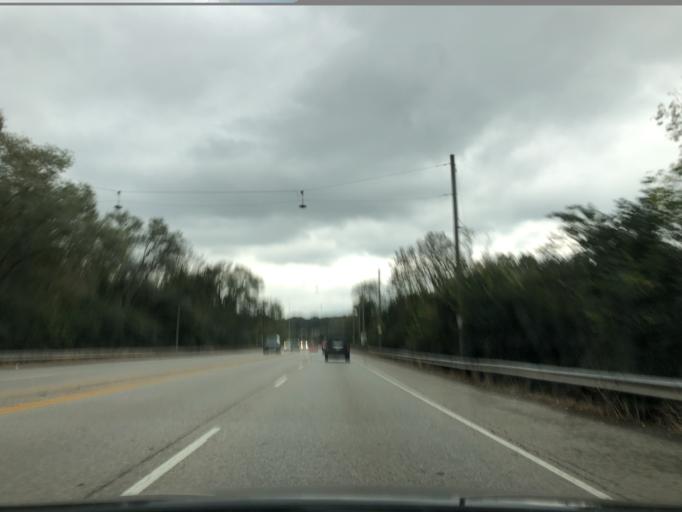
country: US
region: Ohio
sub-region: Hamilton County
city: Turpin Hills
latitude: 39.1116
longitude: -84.4038
